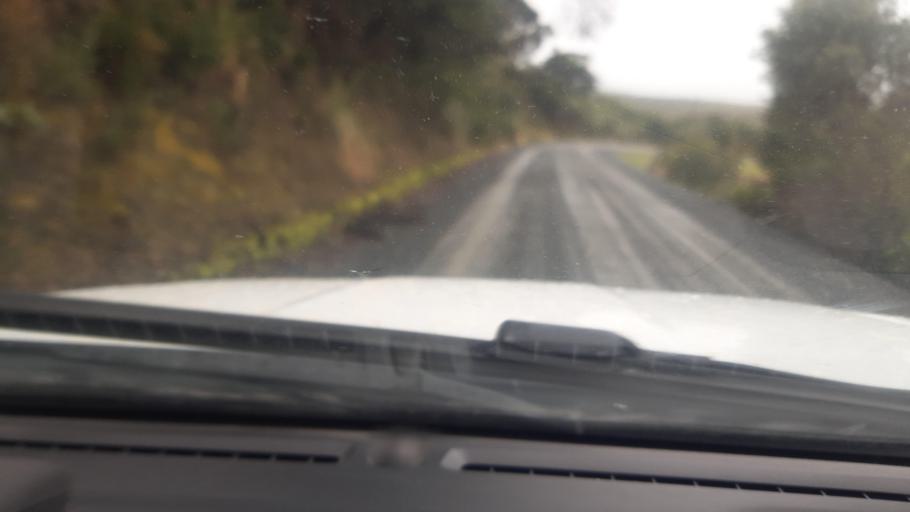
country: NZ
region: Northland
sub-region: Far North District
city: Kaitaia
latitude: -34.9904
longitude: 173.2145
